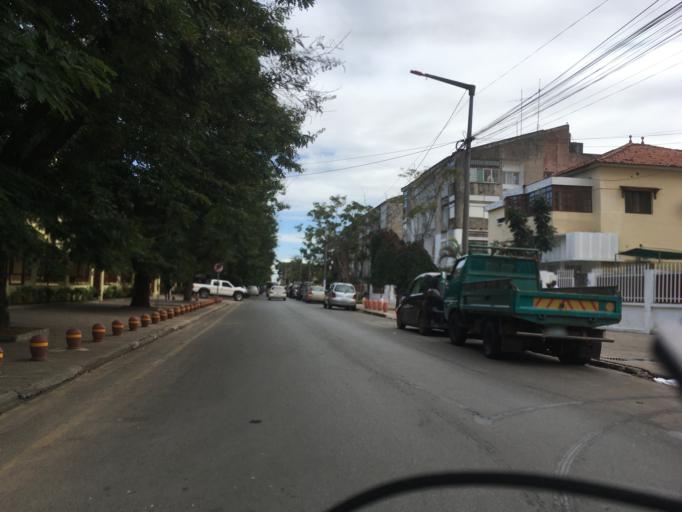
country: MZ
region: Maputo City
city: Maputo
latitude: -25.9633
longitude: 32.5857
